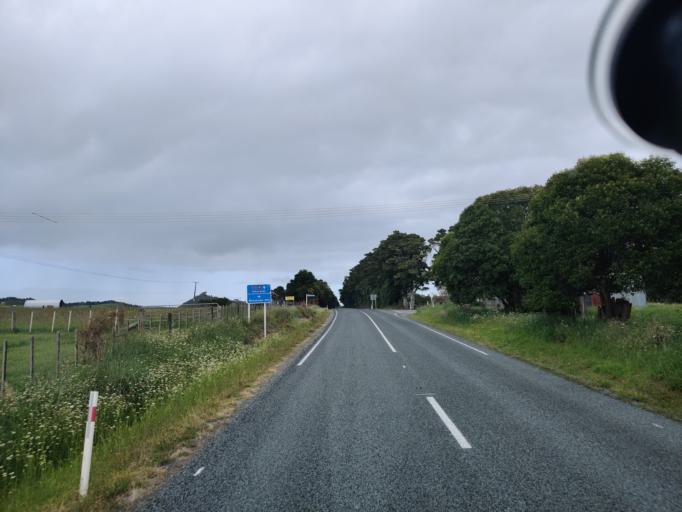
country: NZ
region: Northland
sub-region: Whangarei
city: Ngunguru
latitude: -35.5631
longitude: 174.3893
